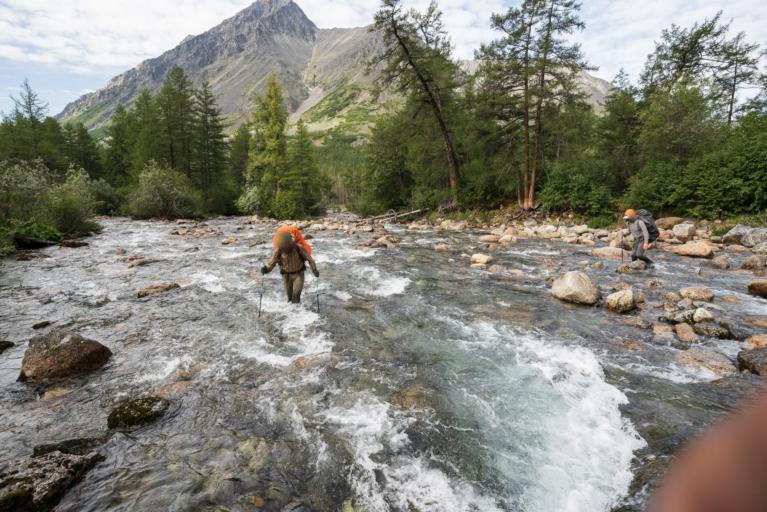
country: RU
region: Transbaikal Territory
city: Chara
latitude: 56.8597
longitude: 117.2872
